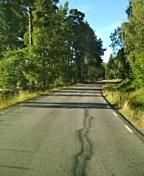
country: SE
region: Uppsala
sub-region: Habo Kommun
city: Balsta
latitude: 59.6928
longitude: 17.5325
